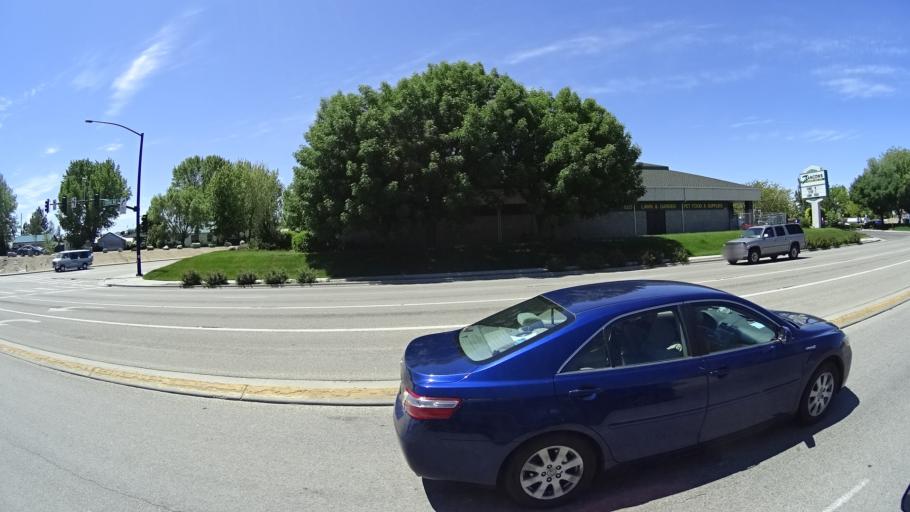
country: US
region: Idaho
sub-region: Ada County
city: Boise
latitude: 43.5683
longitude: -116.1828
